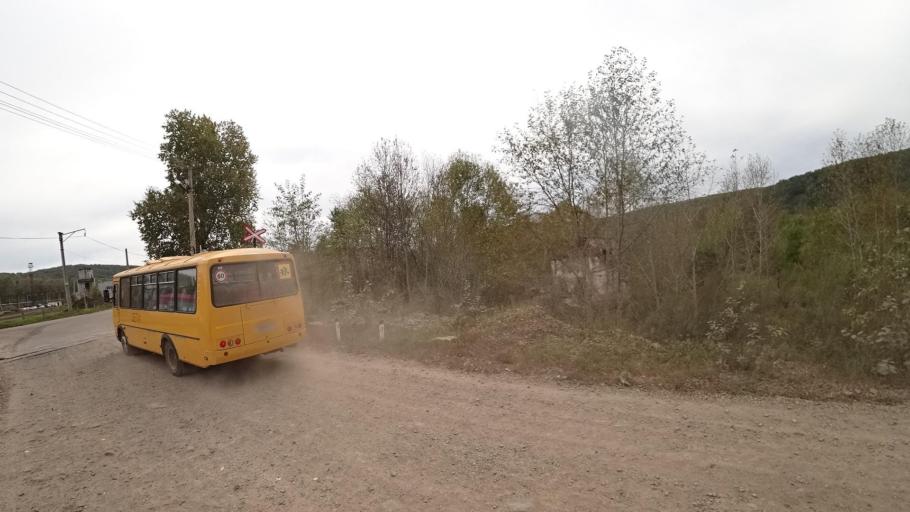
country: RU
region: Jewish Autonomous Oblast
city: Khingansk
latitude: 49.0211
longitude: 131.0544
